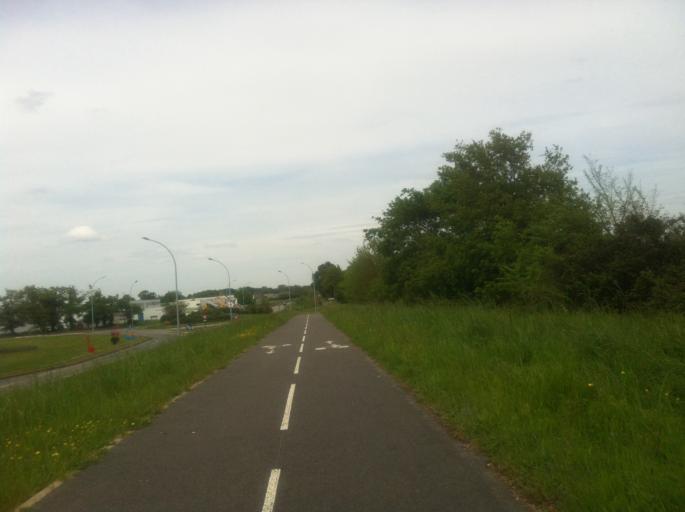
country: FR
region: Brittany
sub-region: Departement d'Ille-et-Vilaine
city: Chartres-de-Bretagne
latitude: 48.0338
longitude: -1.7236
